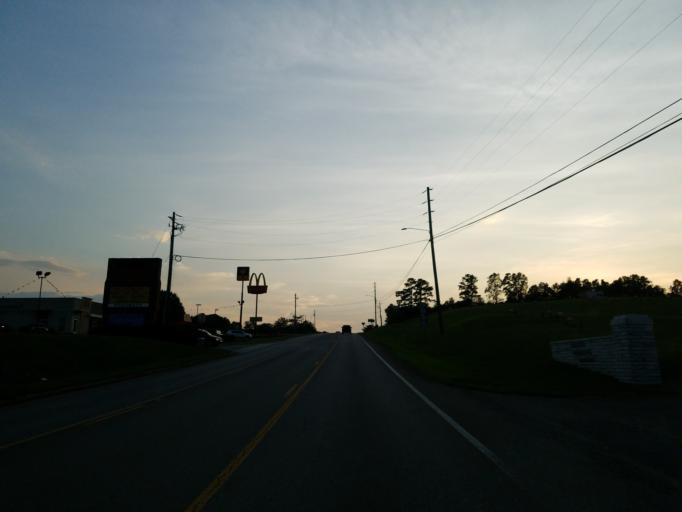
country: US
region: Georgia
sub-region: Pickens County
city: Jasper
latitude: 34.4655
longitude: -84.4546
